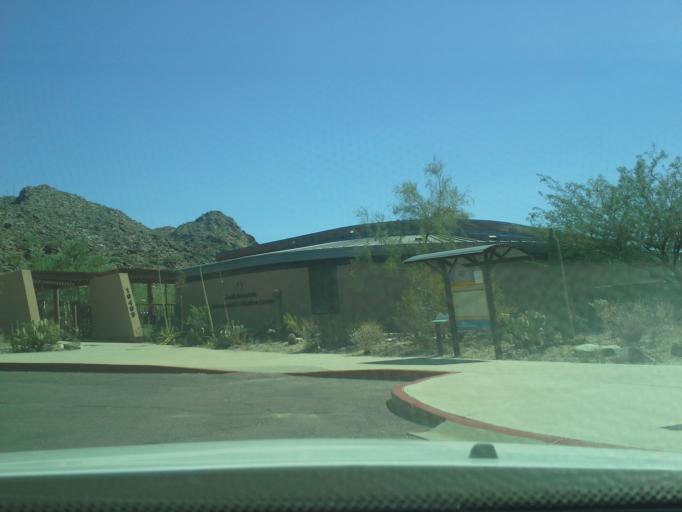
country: US
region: Arizona
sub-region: Maricopa County
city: Laveen
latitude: 33.3511
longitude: -112.0761
